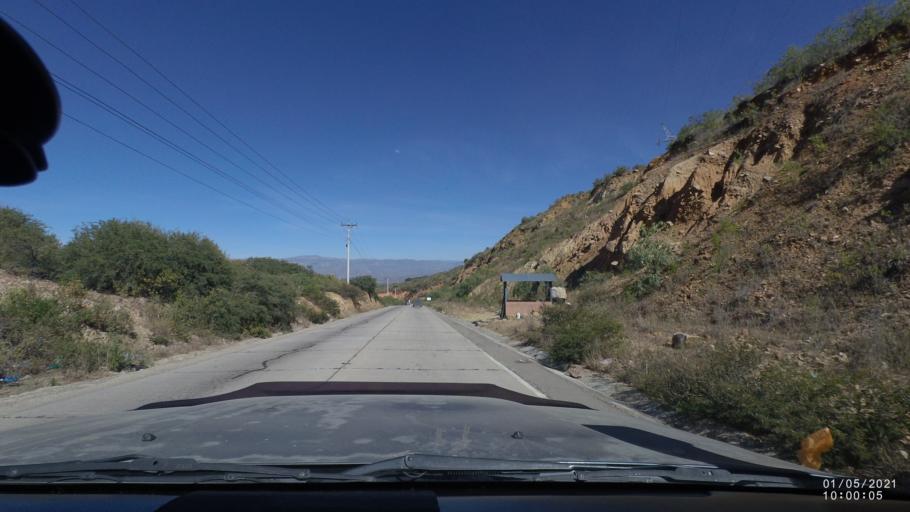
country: BO
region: Cochabamba
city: Cochabamba
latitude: -17.5294
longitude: -66.1940
